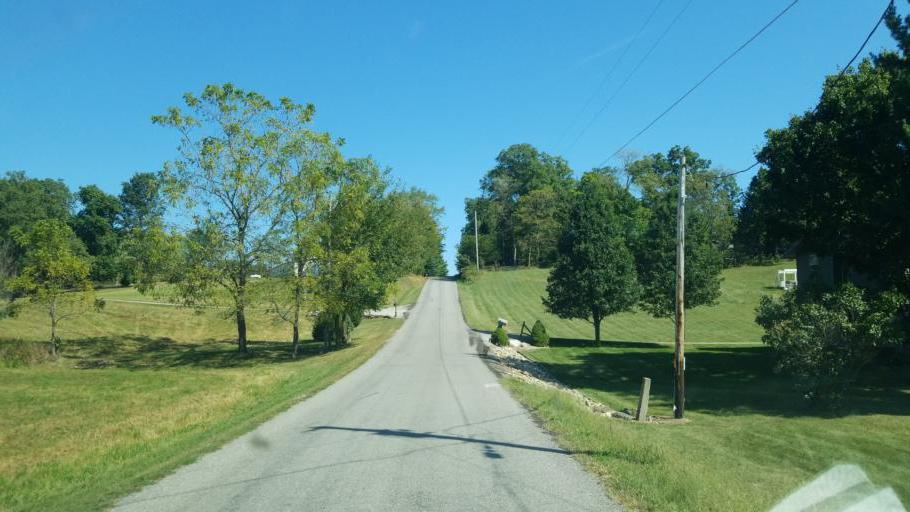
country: US
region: Ohio
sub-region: Logan County
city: West Liberty
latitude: 40.3054
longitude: -83.7330
